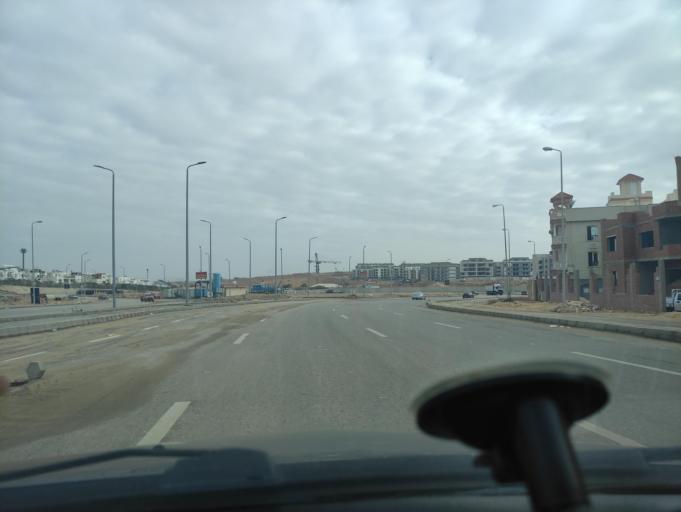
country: EG
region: Muhafazat al Qalyubiyah
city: Al Khankah
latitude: 30.0502
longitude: 31.5306
